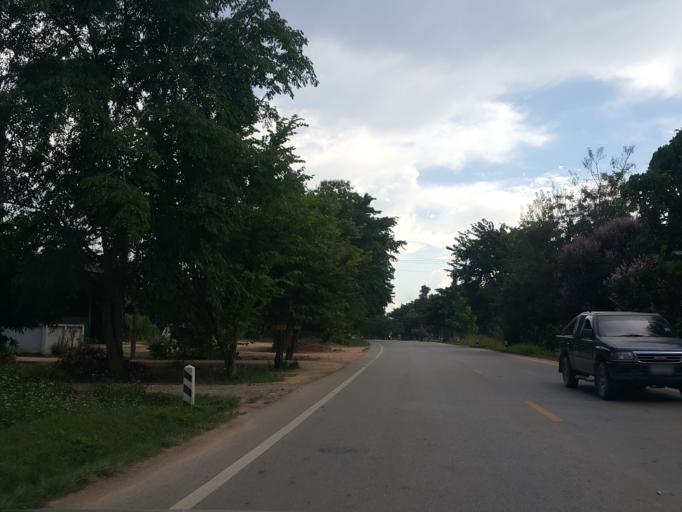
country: TH
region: Chiang Mai
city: Phrao
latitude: 19.3301
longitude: 99.1912
